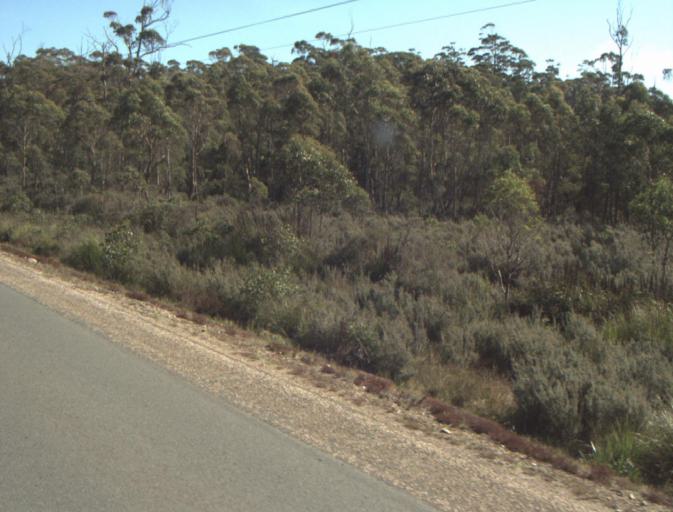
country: AU
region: Tasmania
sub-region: Launceston
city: Mayfield
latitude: -41.3153
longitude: 147.1950
